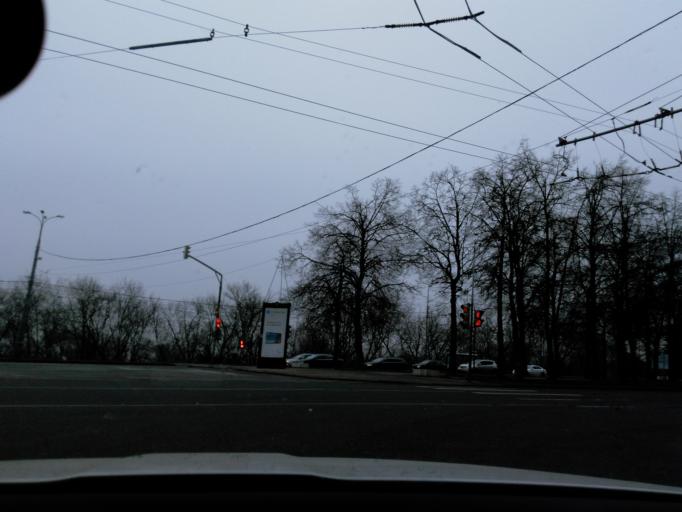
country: RU
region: Moscow
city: Vorob'yovo
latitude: 55.7151
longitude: 37.5356
